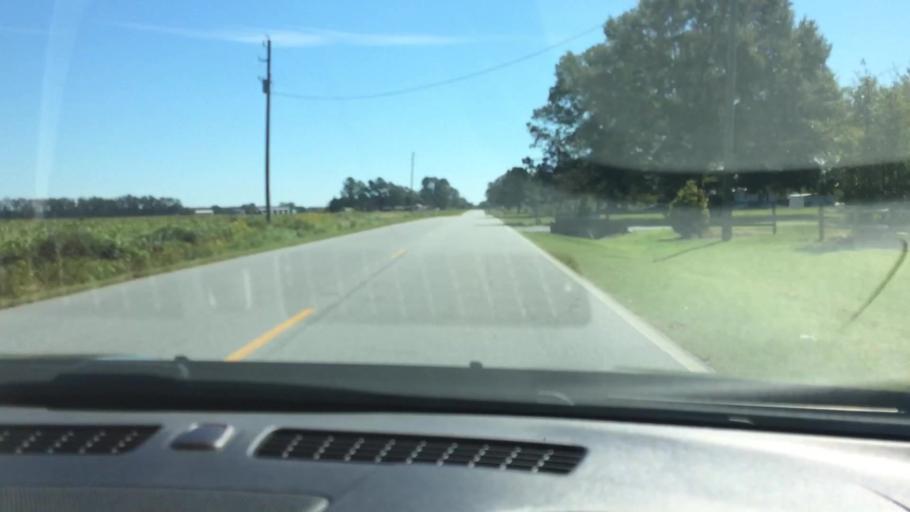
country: US
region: North Carolina
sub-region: Pitt County
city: Grifton
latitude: 35.3907
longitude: -77.3878
